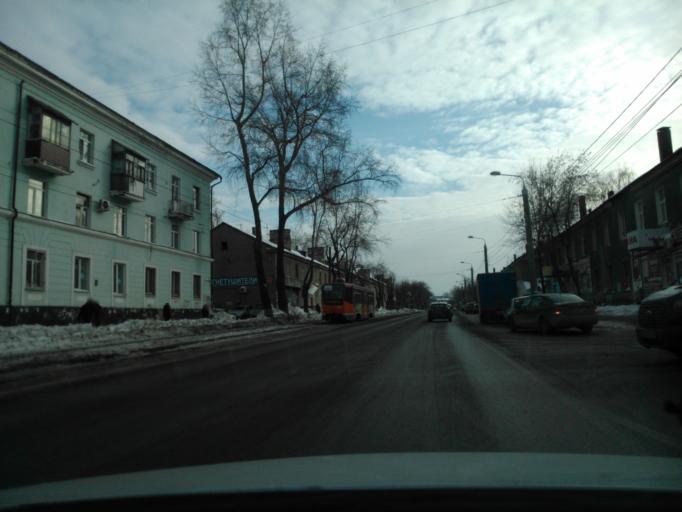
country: RU
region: Perm
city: Perm
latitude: 57.9979
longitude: 56.2433
